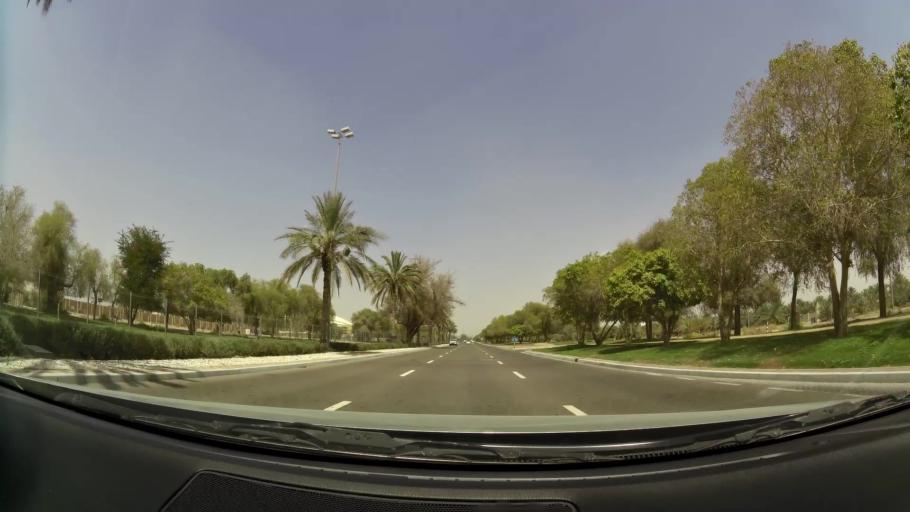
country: AE
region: Abu Dhabi
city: Al Ain
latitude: 24.2427
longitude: 55.7091
